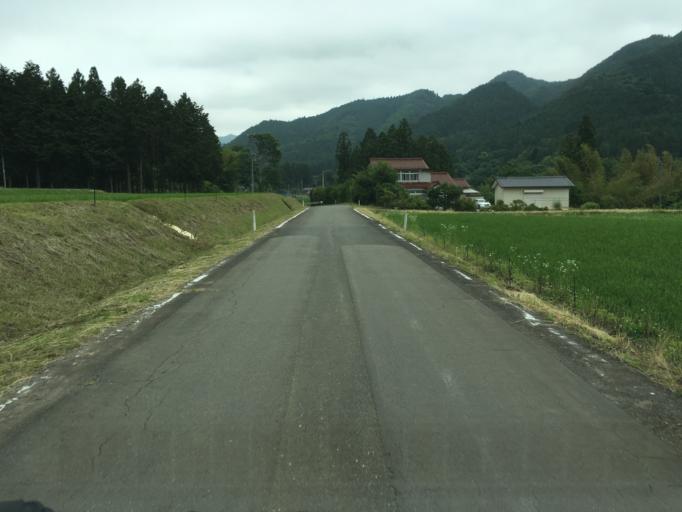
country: JP
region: Miyagi
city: Marumori
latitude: 37.7667
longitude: 140.8443
